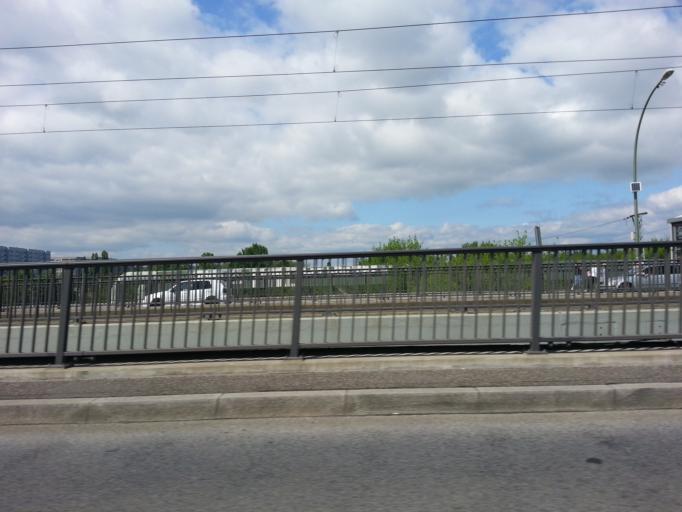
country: DE
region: Berlin
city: Neu-Hohenschoenhausen
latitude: 52.5657
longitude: 13.5121
